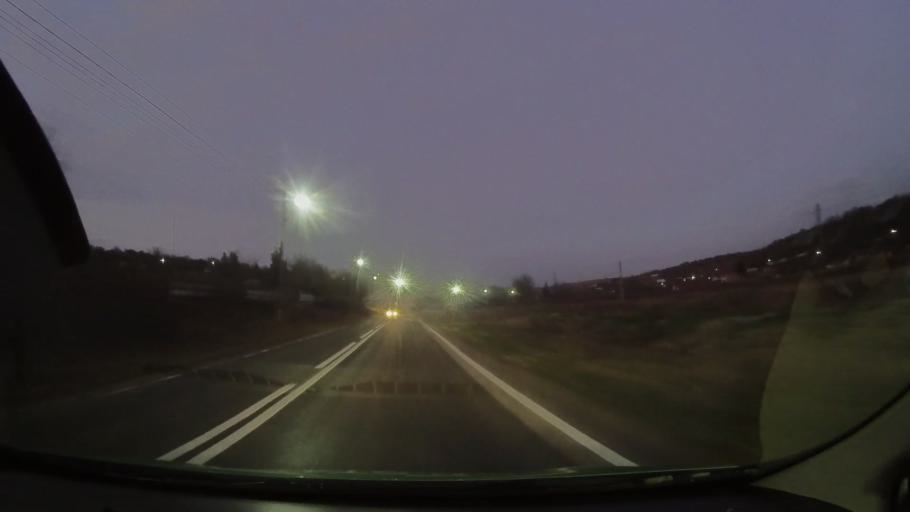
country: RO
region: Constanta
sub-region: Comuna Ion Corvin
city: Ion Corvin
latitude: 44.1087
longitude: 27.8023
